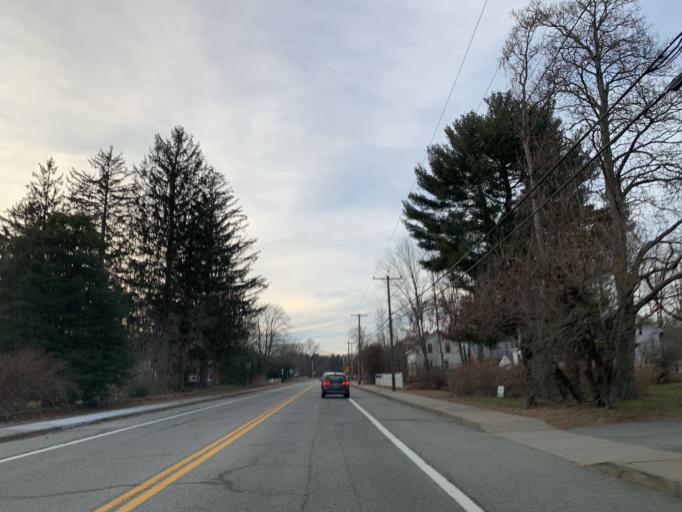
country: US
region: Rhode Island
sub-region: Providence County
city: Chepachet
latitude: 41.9158
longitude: -71.6742
